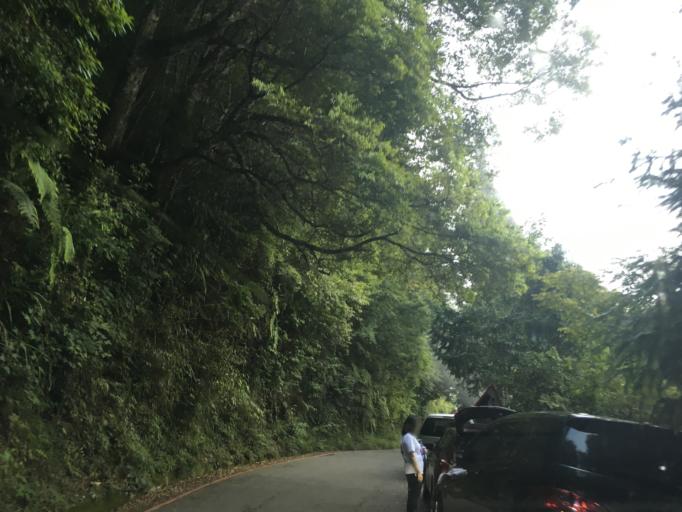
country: TW
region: Taiwan
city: Fengyuan
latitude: 24.2365
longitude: 120.9565
